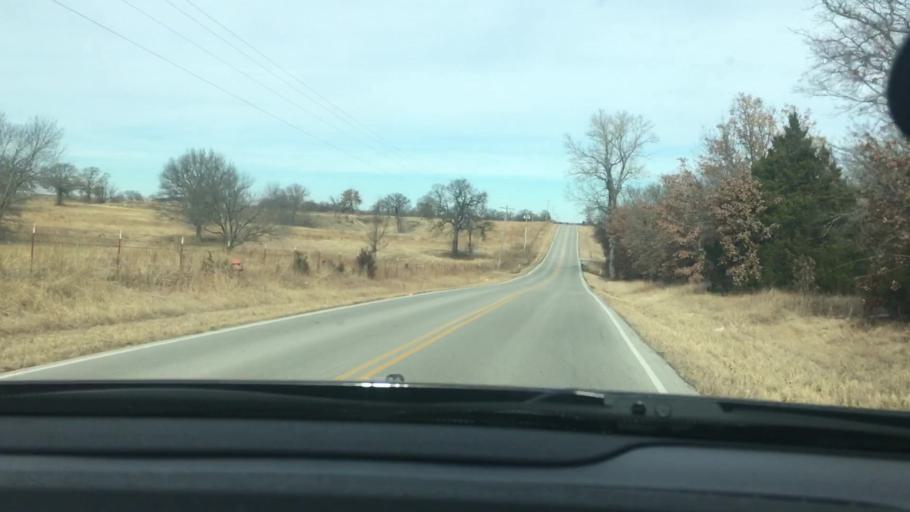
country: US
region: Oklahoma
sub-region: Carter County
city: Ardmore
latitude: 34.1799
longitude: -97.0731
